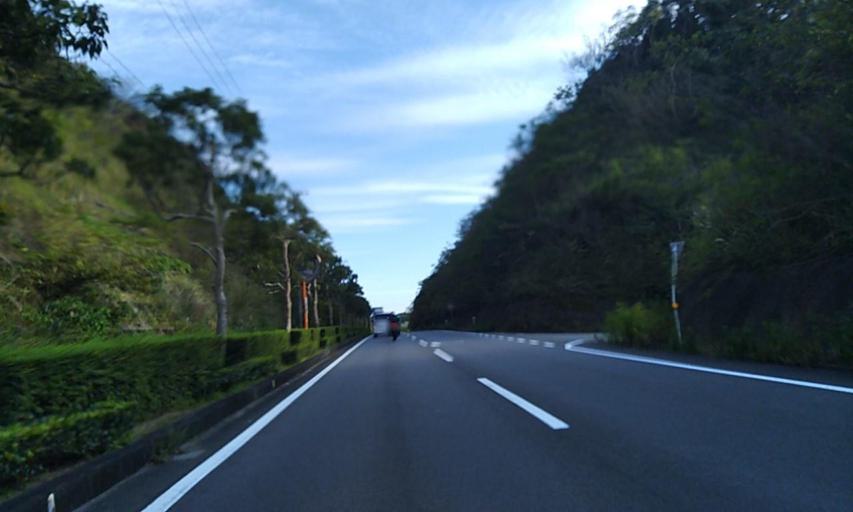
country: JP
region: Mie
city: Toba
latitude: 34.3563
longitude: 136.8058
